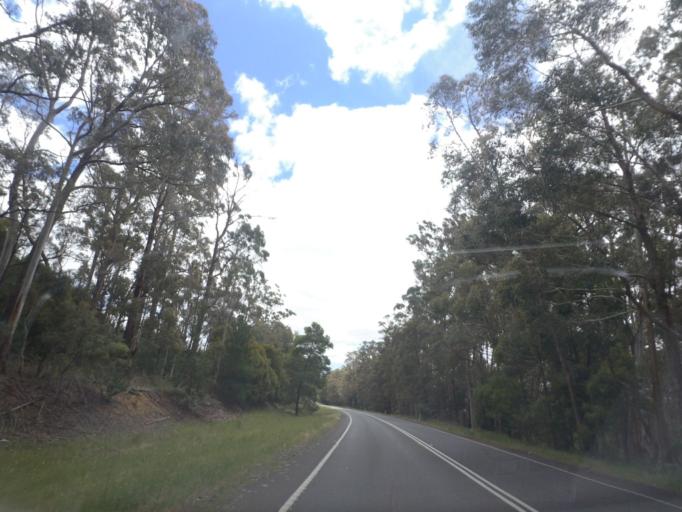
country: AU
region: Victoria
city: Brown Hill
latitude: -37.4942
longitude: 144.1552
